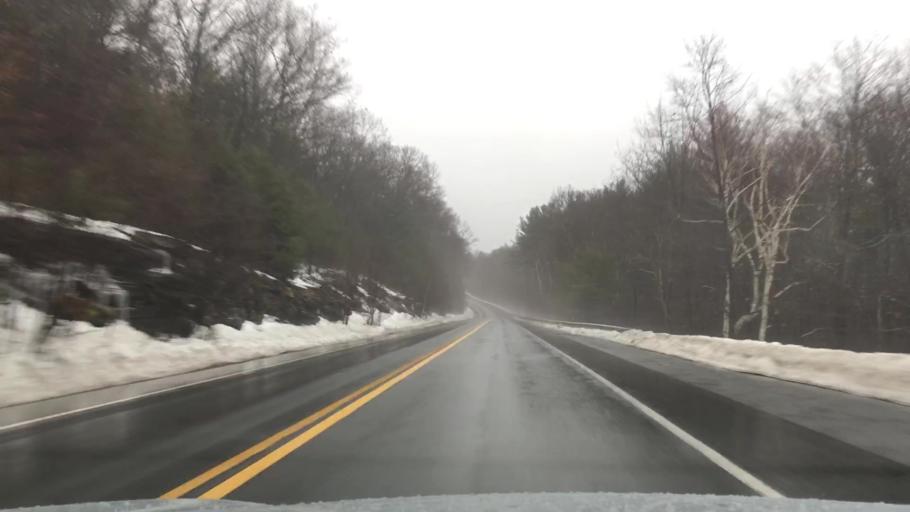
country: US
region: Massachusetts
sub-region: Hampshire County
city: Pelham
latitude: 42.4024
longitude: -72.4038
